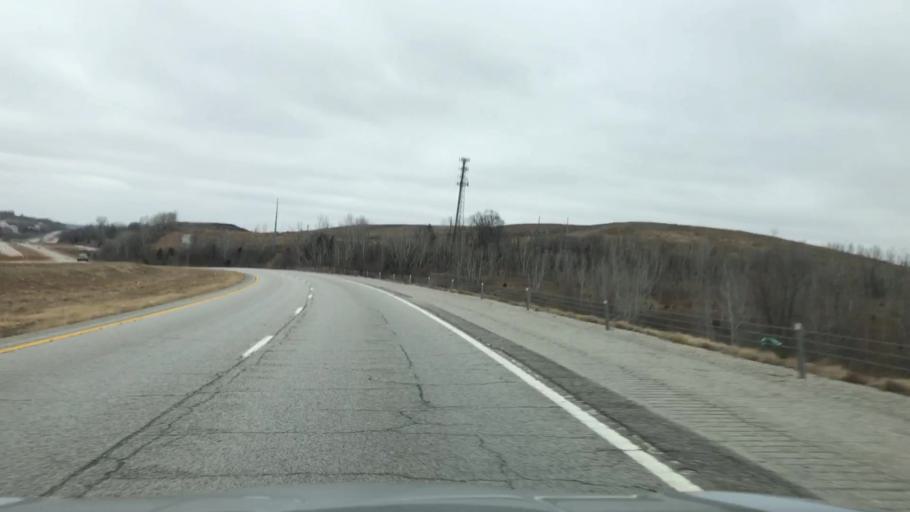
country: US
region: Missouri
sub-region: Jackson County
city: East Independence
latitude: 39.1323
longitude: -94.3836
